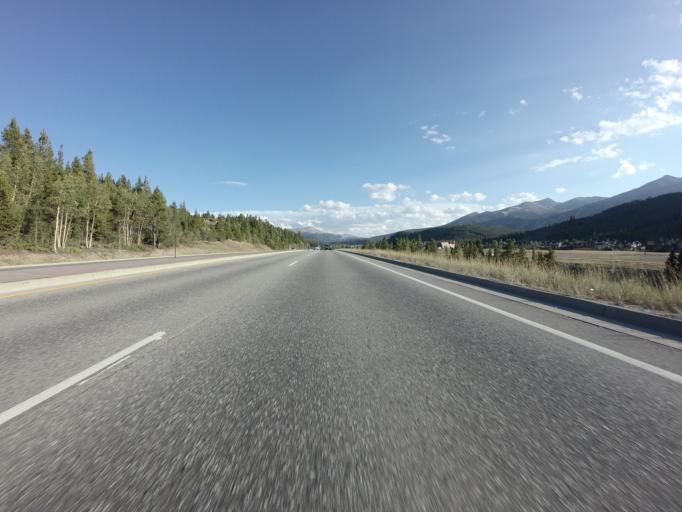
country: US
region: Colorado
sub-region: Summit County
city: Breckenridge
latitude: 39.5046
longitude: -106.0477
